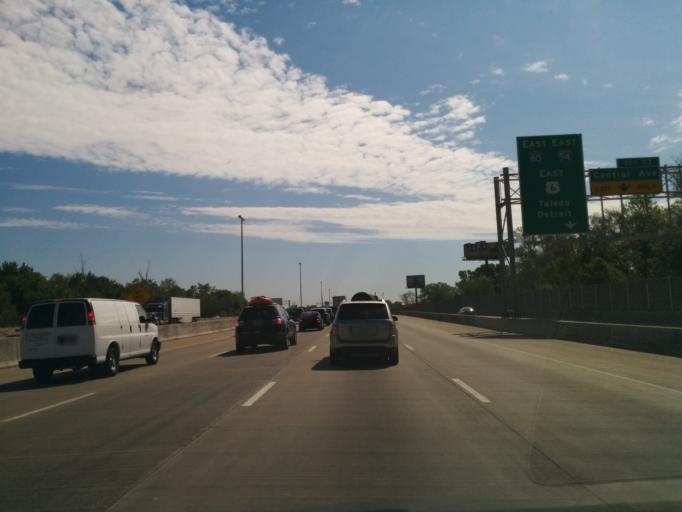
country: US
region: Indiana
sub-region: Lake County
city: New Chicago
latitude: 41.5701
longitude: -87.2946
